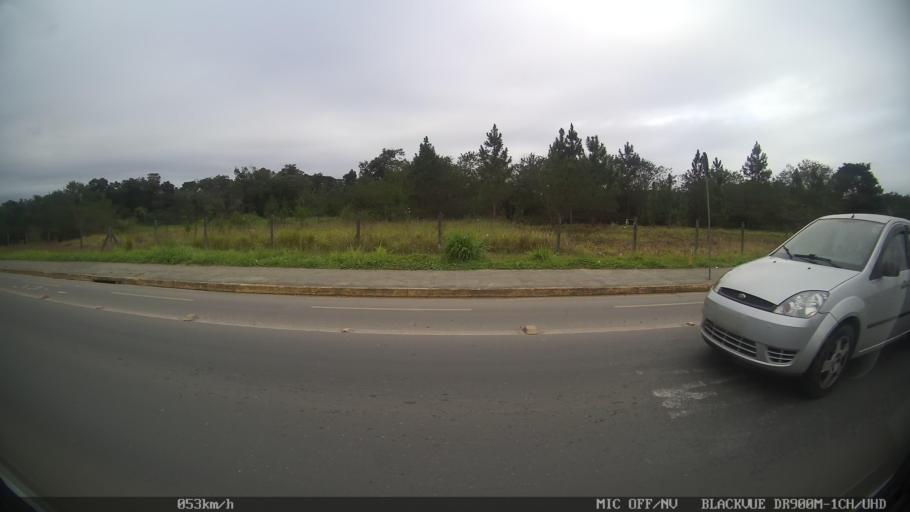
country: BR
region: Santa Catarina
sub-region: Joinville
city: Joinville
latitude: -26.3377
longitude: -48.8928
